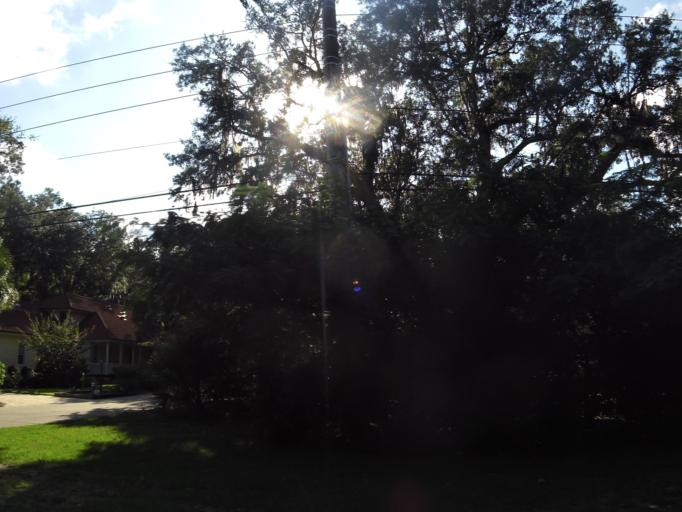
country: US
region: Georgia
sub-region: Glynn County
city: Saint Simon Mills
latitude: 31.2029
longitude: -81.3760
